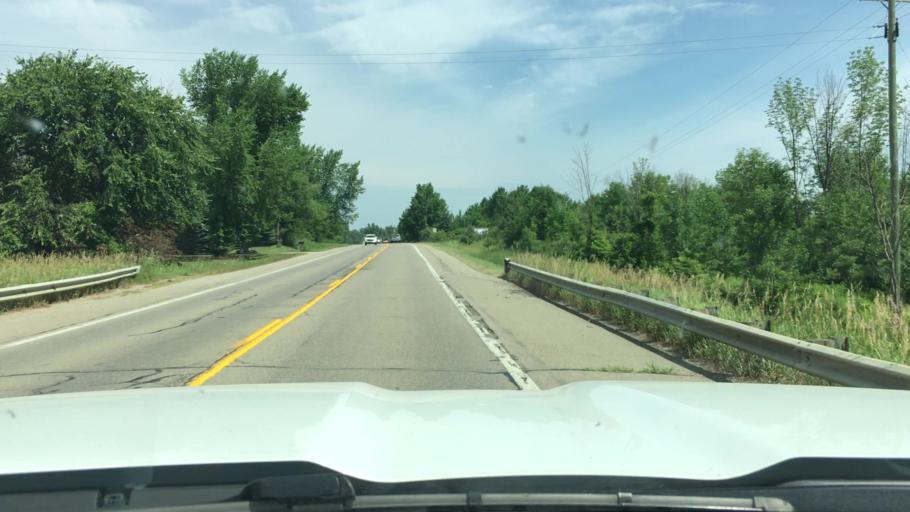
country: US
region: Michigan
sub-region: Sanilac County
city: Brown City
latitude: 43.1452
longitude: -83.0742
